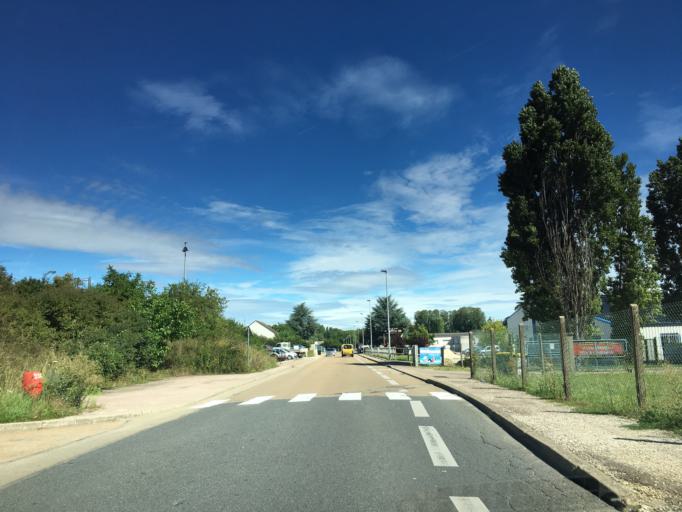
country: FR
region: Bourgogne
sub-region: Departement de l'Yonne
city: Auxerre
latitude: 47.8139
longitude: 3.5763
